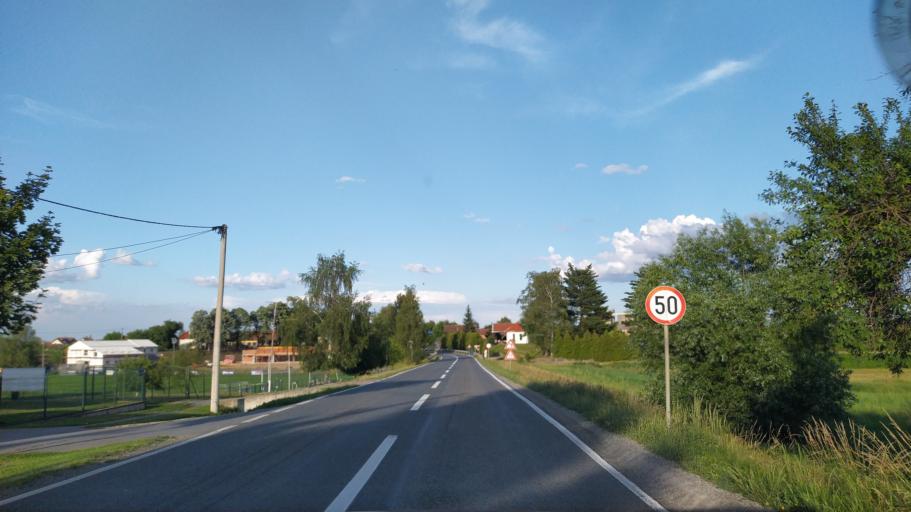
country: HR
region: Virovitick-Podravska
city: Cacinci
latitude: 45.5998
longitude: 17.8591
